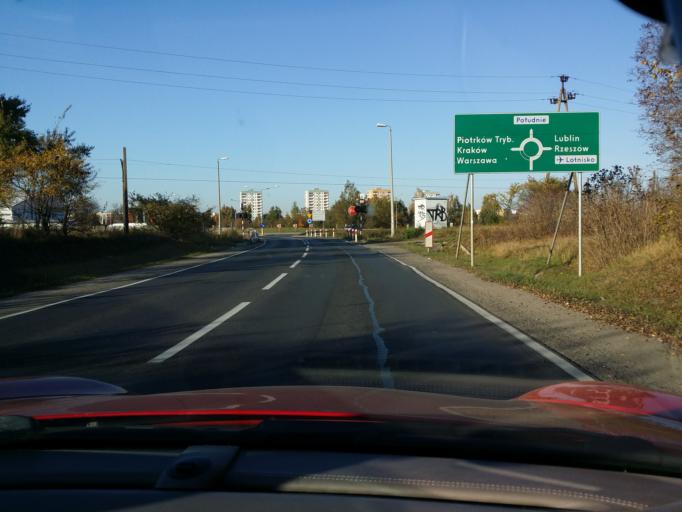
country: PL
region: Masovian Voivodeship
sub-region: Powiat radomski
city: Trablice
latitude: 51.3580
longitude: 21.1305
